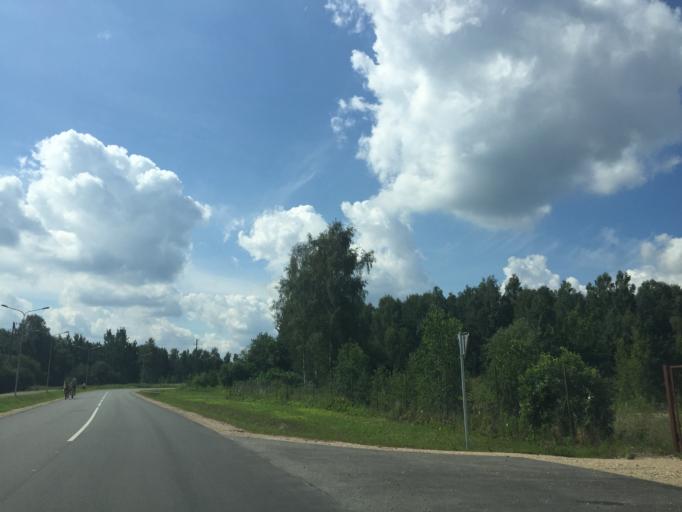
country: LV
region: Kekava
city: Balozi
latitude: 56.8684
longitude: 24.1064
